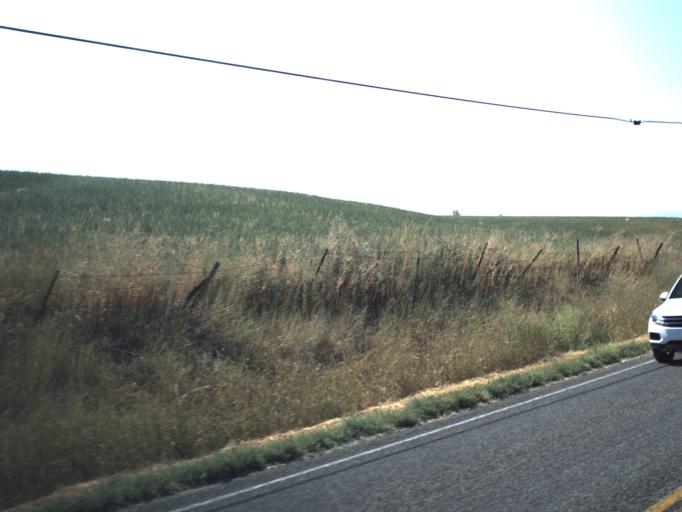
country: US
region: Utah
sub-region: Cache County
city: Hyrum
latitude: 41.5954
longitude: -111.8359
